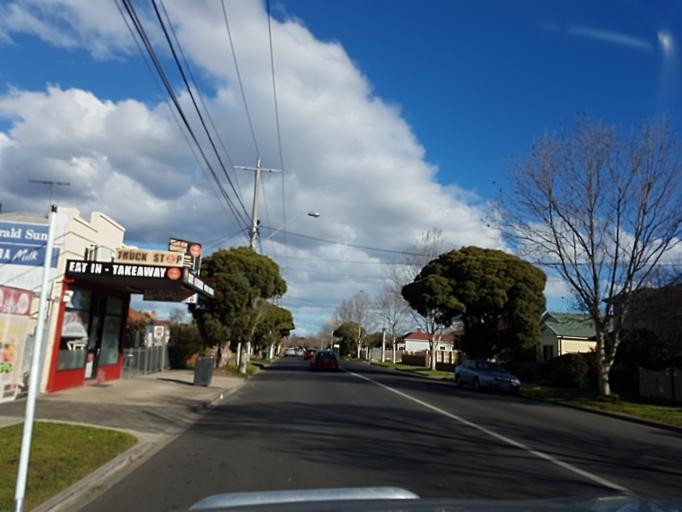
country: AU
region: Victoria
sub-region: Darebin
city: Fairfield
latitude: -37.7710
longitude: 145.0266
